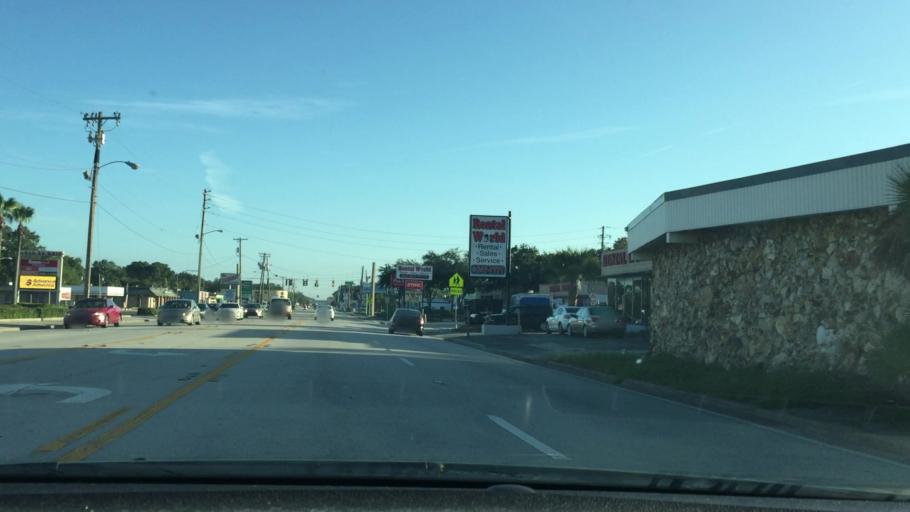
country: US
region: Florida
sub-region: Osceola County
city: Kissimmee
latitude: 28.3072
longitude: -81.4037
